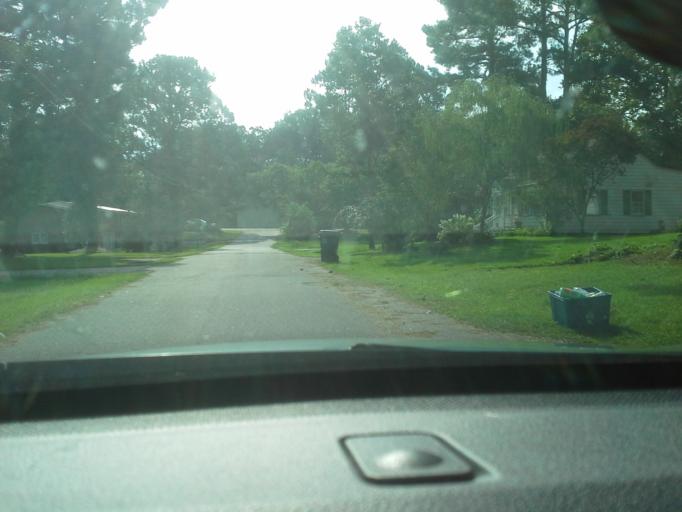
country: US
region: North Carolina
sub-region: Washington County
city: Plymouth
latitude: 35.8607
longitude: -76.7601
